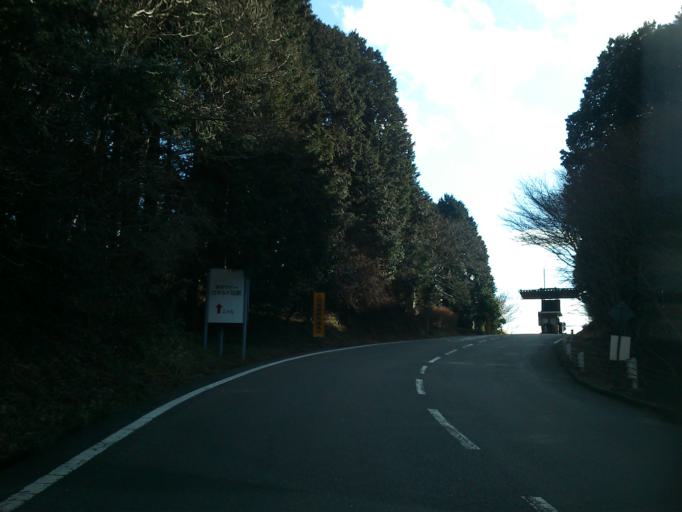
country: JP
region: Shiga Prefecture
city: Otsu-shi
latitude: 35.0555
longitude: 135.8338
